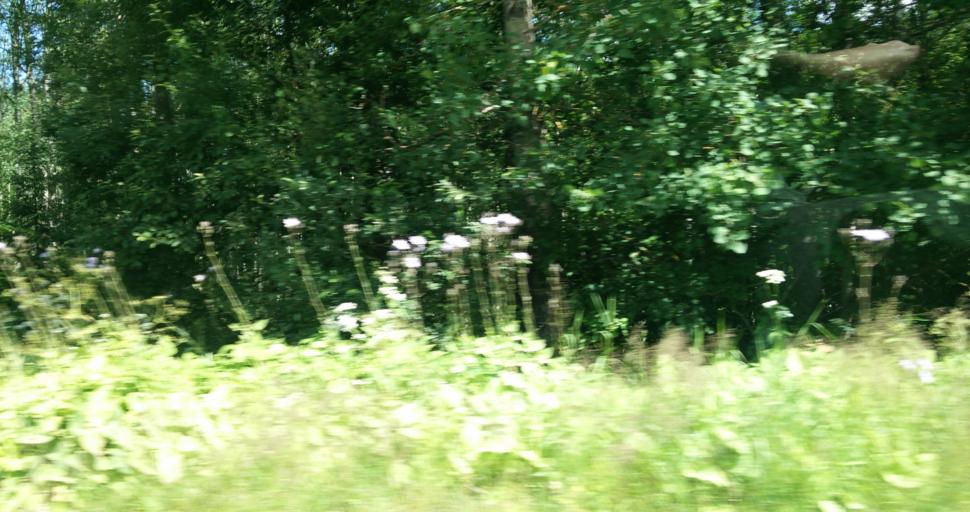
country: SE
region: Vaermland
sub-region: Hagfors Kommun
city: Hagfors
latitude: 60.0192
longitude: 13.6839
